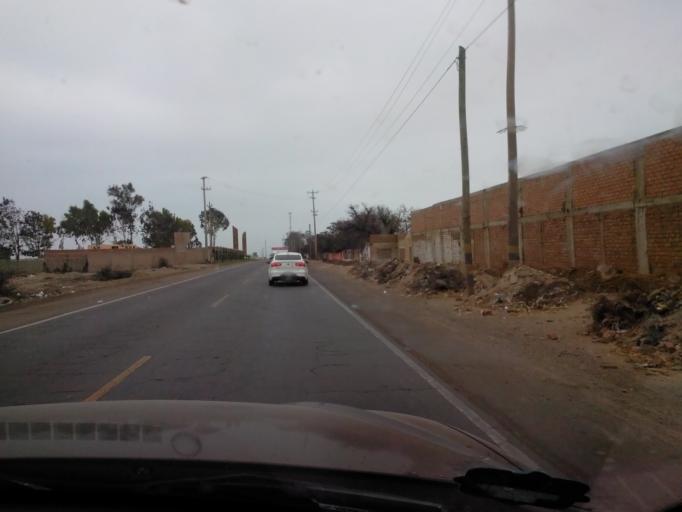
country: PE
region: Ica
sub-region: Provincia de Chincha
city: Sunampe
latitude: -13.4123
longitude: -76.1794
